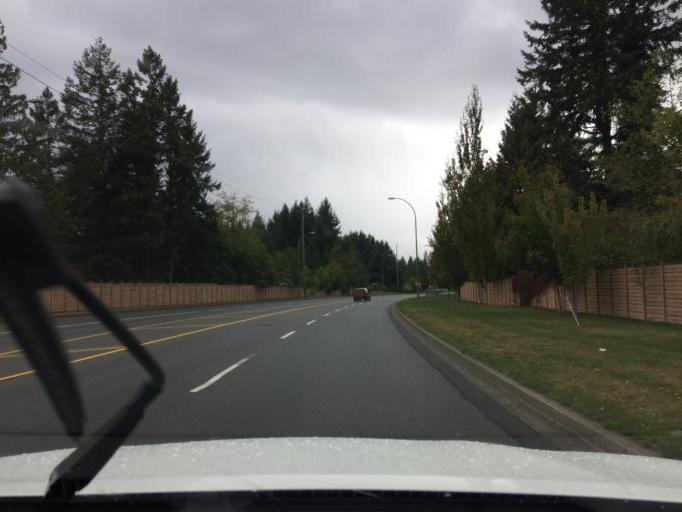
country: CA
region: British Columbia
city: Courtenay
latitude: 49.7155
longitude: -124.9887
